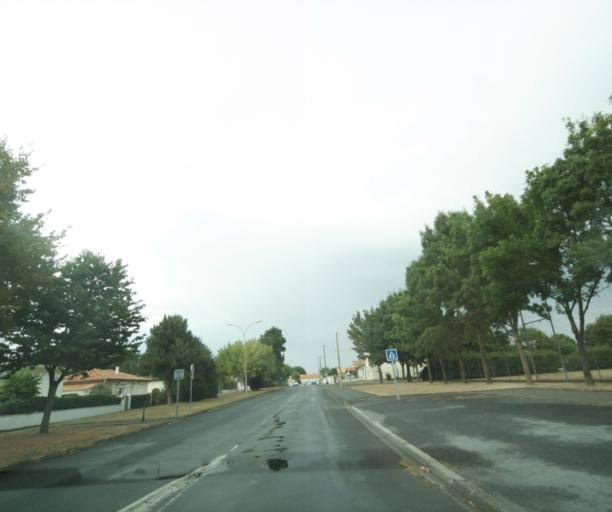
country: FR
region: Poitou-Charentes
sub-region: Departement de la Charente-Maritime
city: Tonnay-Charente
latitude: 45.9460
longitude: -0.9104
